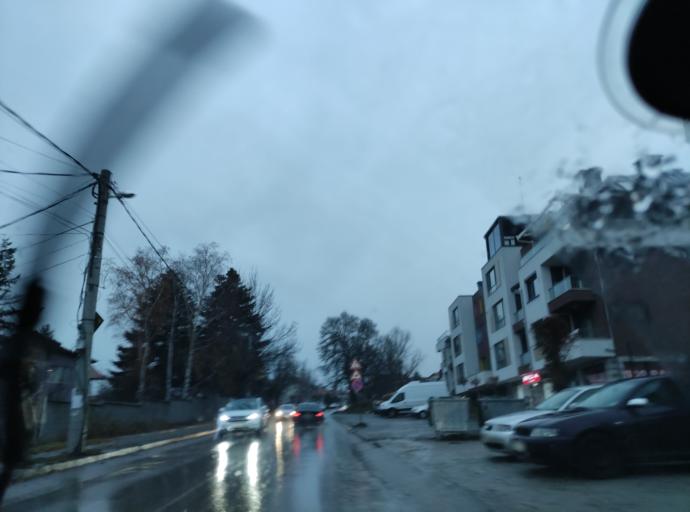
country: BG
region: Sofia-Capital
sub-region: Stolichna Obshtina
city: Sofia
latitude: 42.6322
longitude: 23.3124
